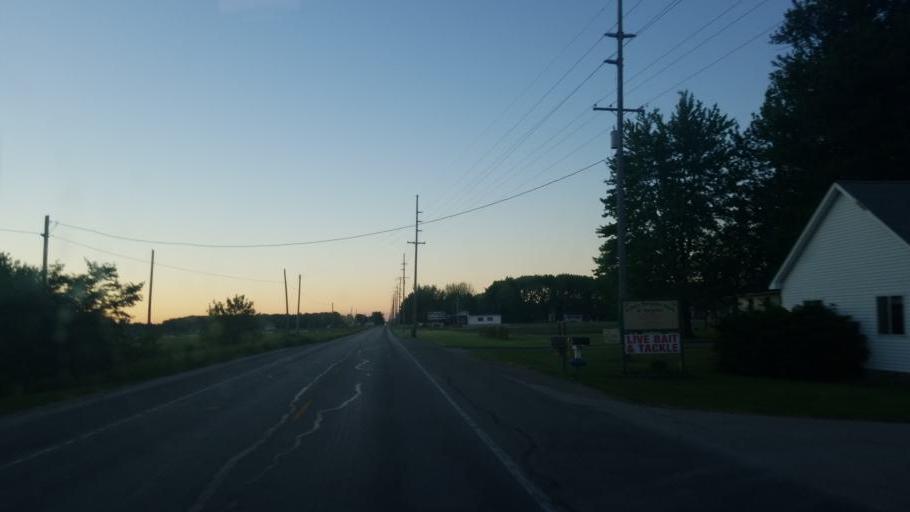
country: US
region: Indiana
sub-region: Elkhart County
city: Nappanee
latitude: 41.3739
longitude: -86.0006
